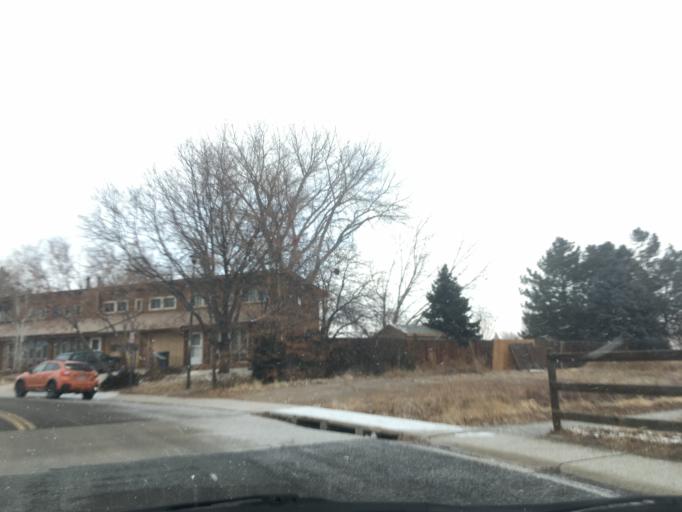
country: US
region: Colorado
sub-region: Boulder County
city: Lafayette
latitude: 39.9899
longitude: -105.0792
